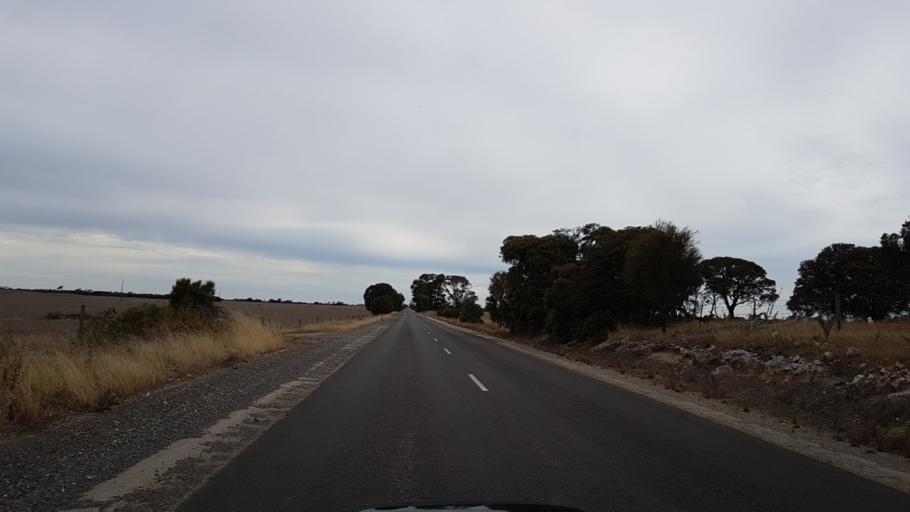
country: AU
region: South Australia
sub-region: Yorke Peninsula
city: Honiton
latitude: -34.9851
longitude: 137.1835
